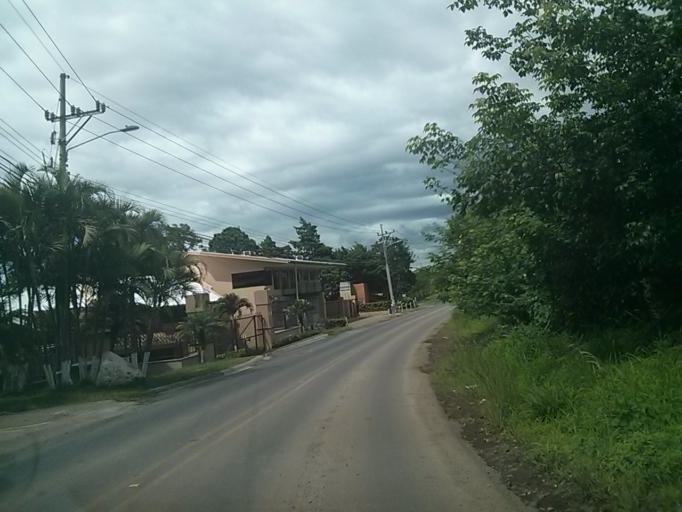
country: CR
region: Heredia
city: La Asuncion
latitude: 9.9646
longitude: -84.1818
